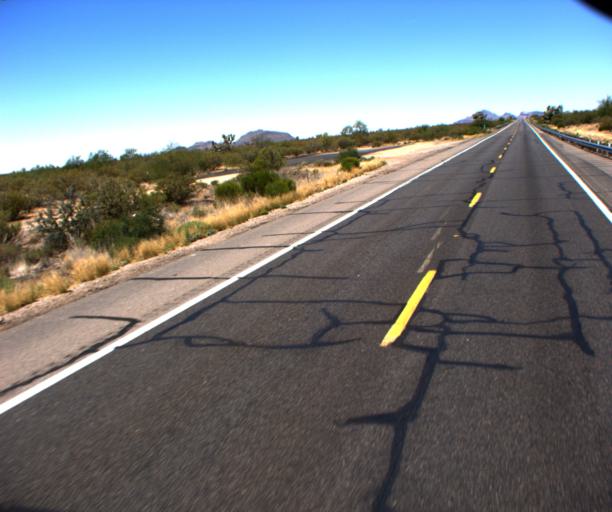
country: US
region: Arizona
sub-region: Yavapai County
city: Congress
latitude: 34.1767
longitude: -113.0287
